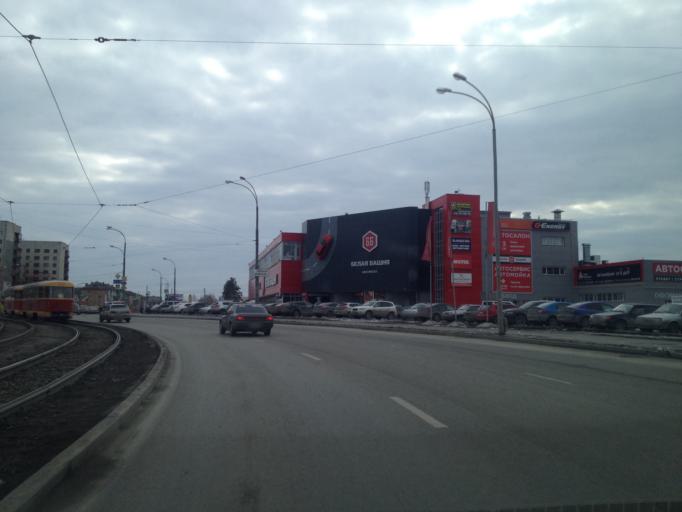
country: RU
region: Sverdlovsk
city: Yekaterinburg
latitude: 56.8935
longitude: 60.5720
